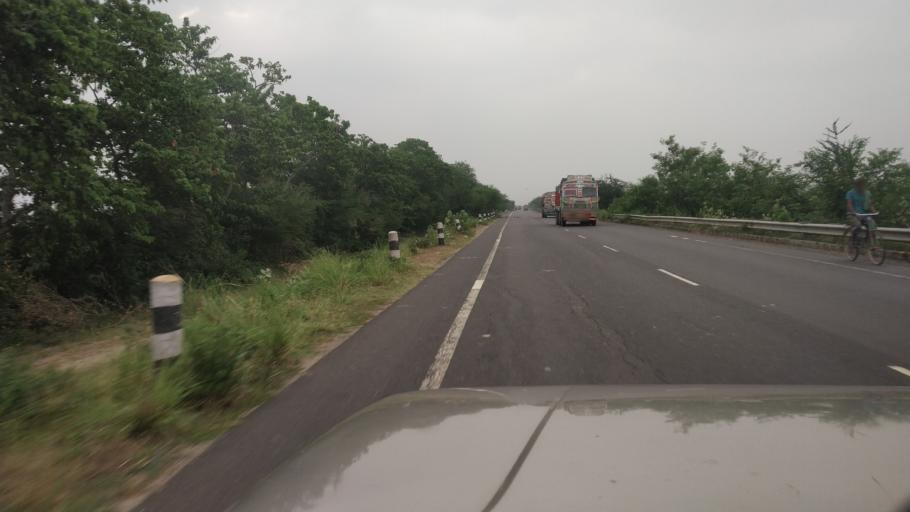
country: IN
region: Bihar
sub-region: Munger
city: Bariarpur
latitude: 25.4045
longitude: 86.7869
